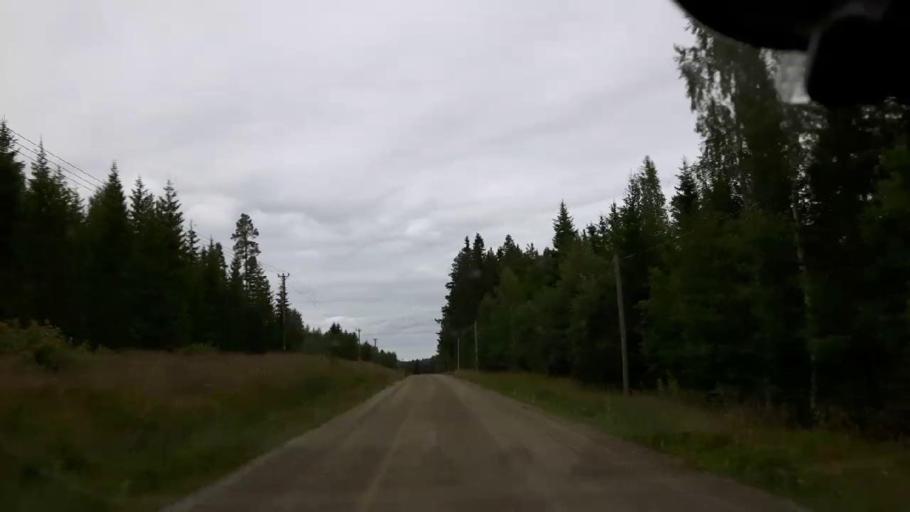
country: SE
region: Jaemtland
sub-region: Braecke Kommun
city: Braecke
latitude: 63.0243
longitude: 15.3724
